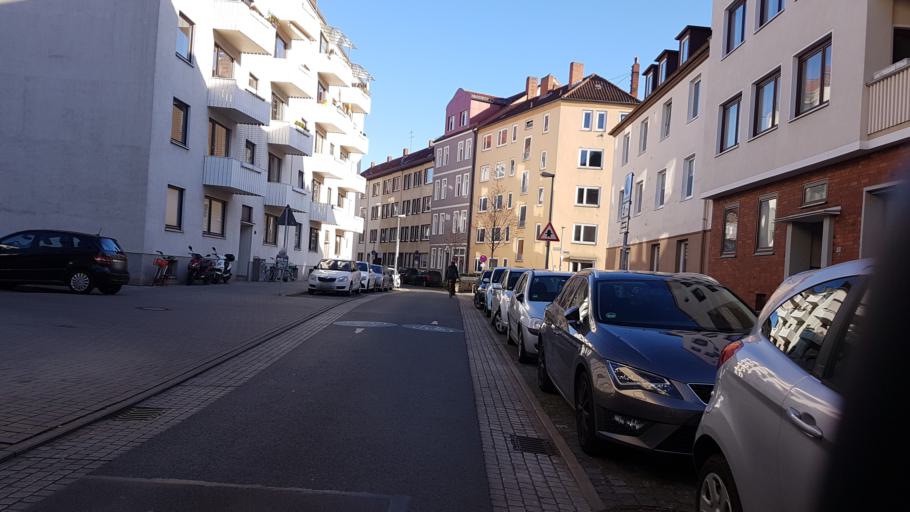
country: DE
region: Lower Saxony
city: Hannover
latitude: 52.3656
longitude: 9.7544
